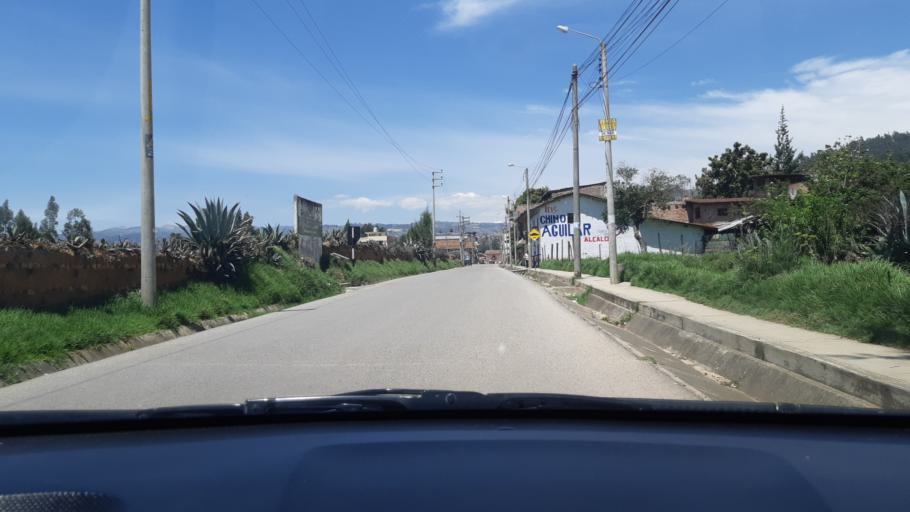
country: PE
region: Cajamarca
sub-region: Provincia de Cajamarca
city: Llacanora
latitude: -7.1713
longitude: -78.4577
